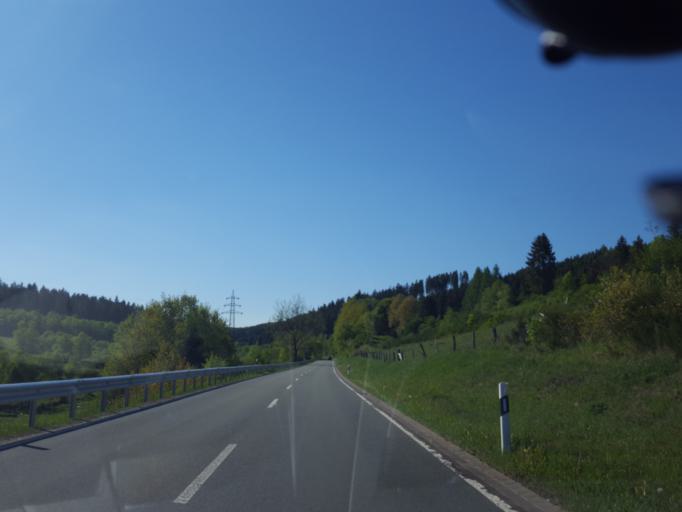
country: DE
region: North Rhine-Westphalia
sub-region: Regierungsbezirk Arnsberg
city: Winterberg
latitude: 51.2076
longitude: 8.5068
